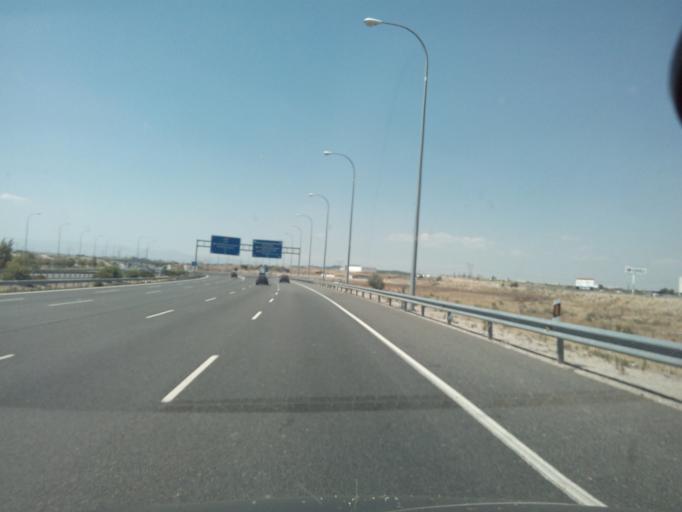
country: ES
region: Madrid
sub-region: Provincia de Madrid
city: San Fernando de Henares
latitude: 40.4282
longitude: -3.4997
